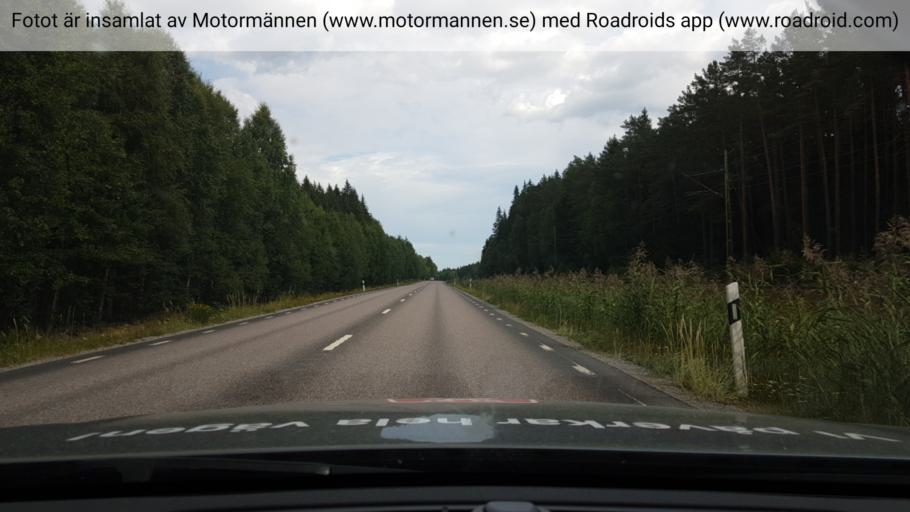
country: SE
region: Uppsala
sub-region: Enkopings Kommun
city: Orsundsbro
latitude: 59.8828
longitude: 17.2225
